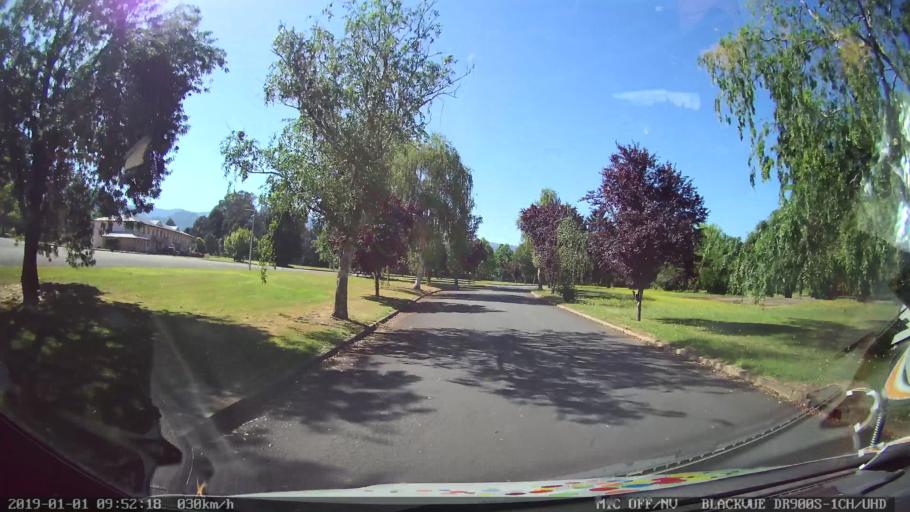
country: AU
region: New South Wales
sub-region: Snowy River
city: Jindabyne
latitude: -36.2174
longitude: 148.1240
